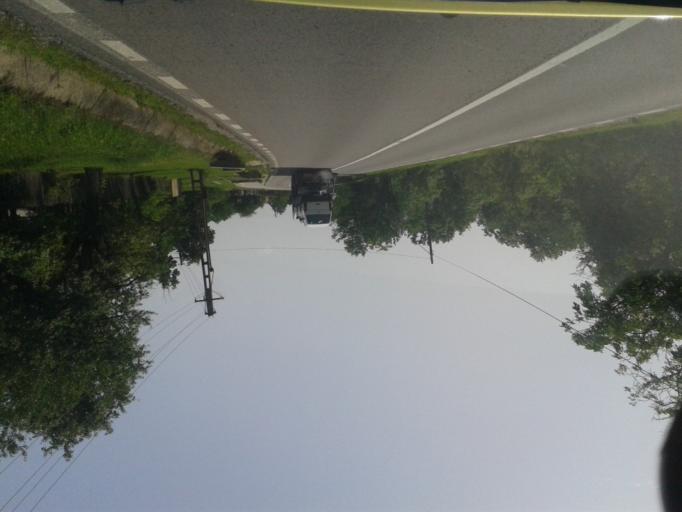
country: RO
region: Arges
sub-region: Comuna Cotmeana
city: Cotmeana
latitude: 44.9860
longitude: 24.6477
